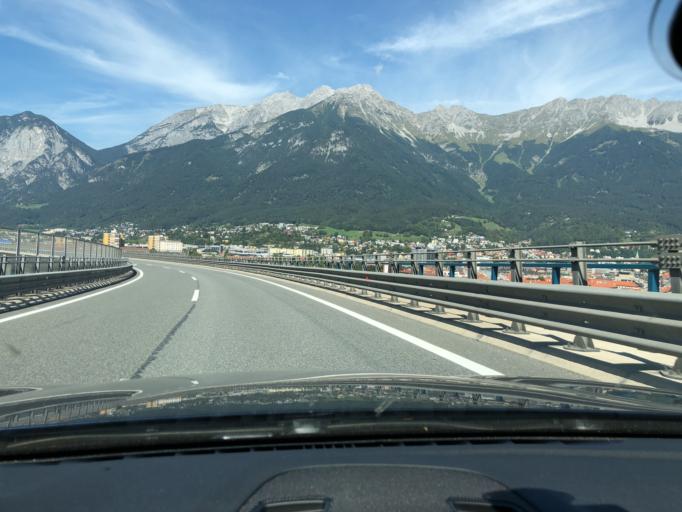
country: AT
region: Tyrol
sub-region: Innsbruck Stadt
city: Innsbruck
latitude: 47.2527
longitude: 11.3913
